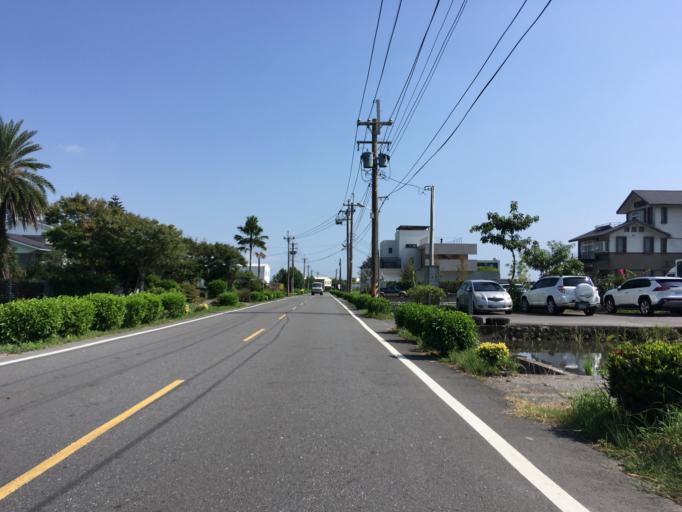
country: TW
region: Taiwan
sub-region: Yilan
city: Yilan
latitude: 24.6767
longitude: 121.7337
